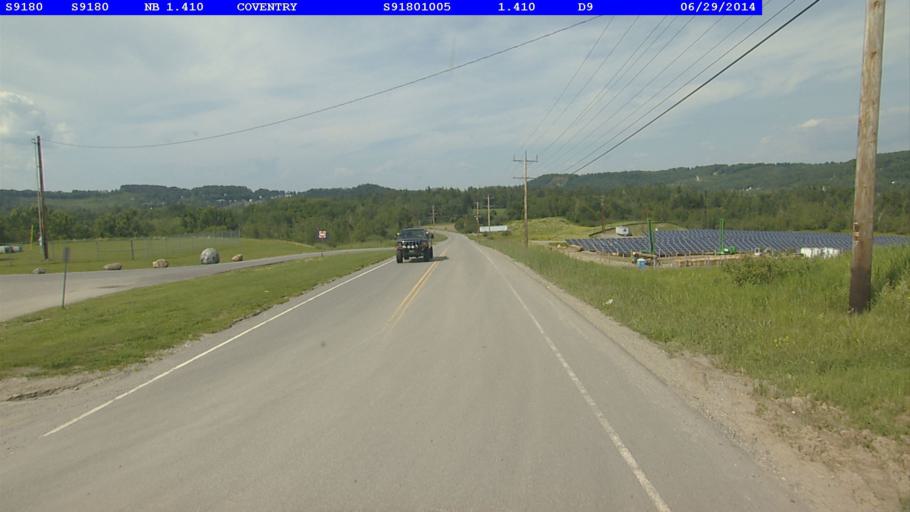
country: US
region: Vermont
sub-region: Orleans County
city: Newport
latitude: 44.9087
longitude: -72.2209
